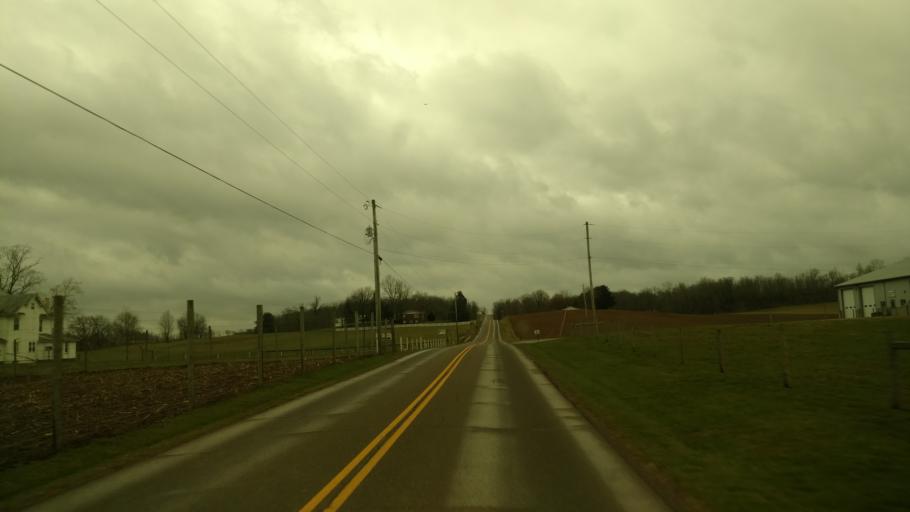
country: US
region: Ohio
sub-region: Holmes County
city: Millersburg
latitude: 40.6043
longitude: -81.8200
